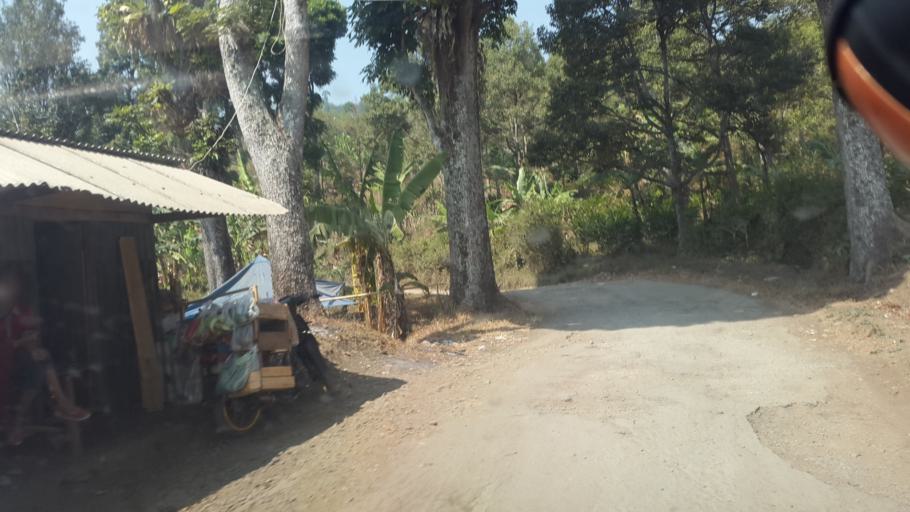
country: ID
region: West Java
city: Pasirreungit
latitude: -6.9956
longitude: 107.0194
